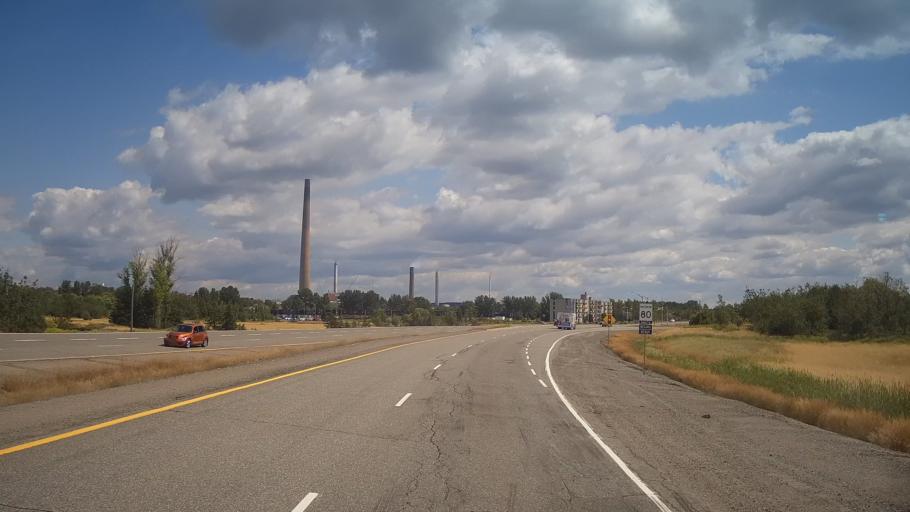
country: CA
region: Ontario
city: Greater Sudbury
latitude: 46.4643
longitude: -81.0775
